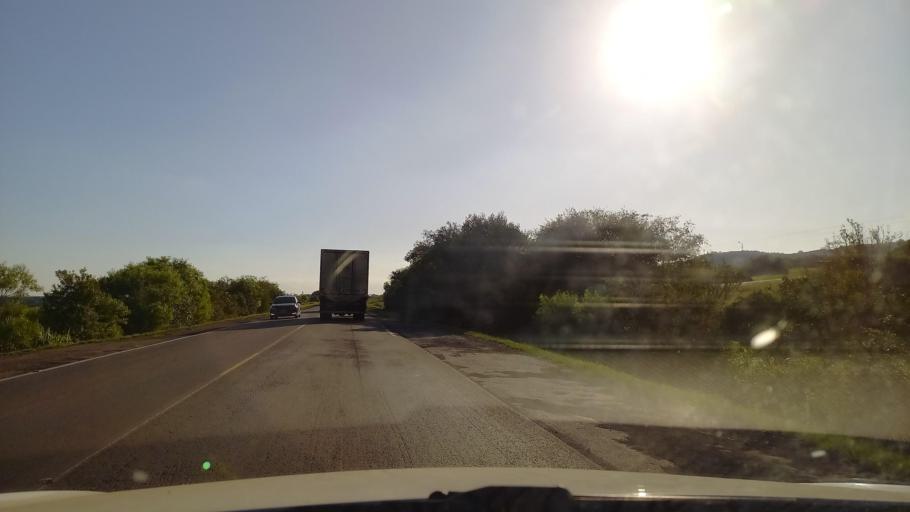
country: BR
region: Rio Grande do Sul
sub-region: Taquari
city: Taquari
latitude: -29.7028
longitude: -51.9200
